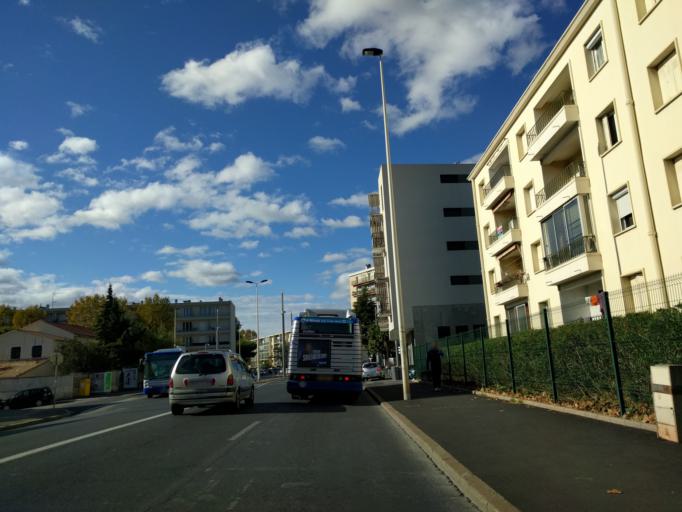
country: FR
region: Languedoc-Roussillon
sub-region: Departement de l'Herault
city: Montpellier
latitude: 43.6267
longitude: 3.8675
